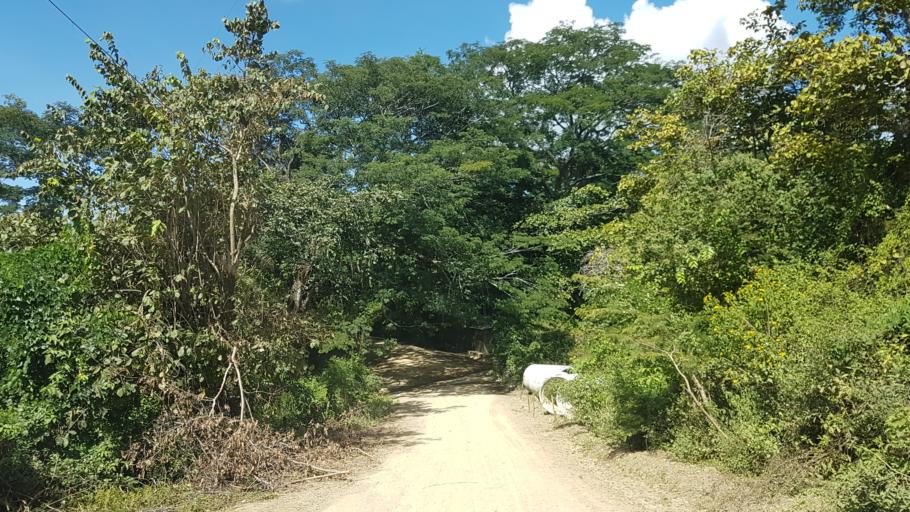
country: HN
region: El Paraiso
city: Oropoli
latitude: 13.7357
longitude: -86.6963
